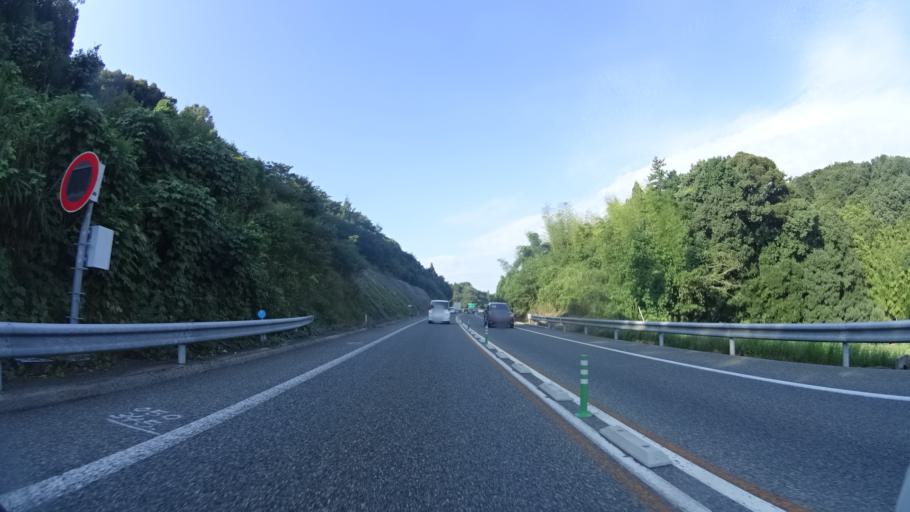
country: JP
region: Shimane
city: Hiratacho
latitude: 35.4009
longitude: 132.9263
